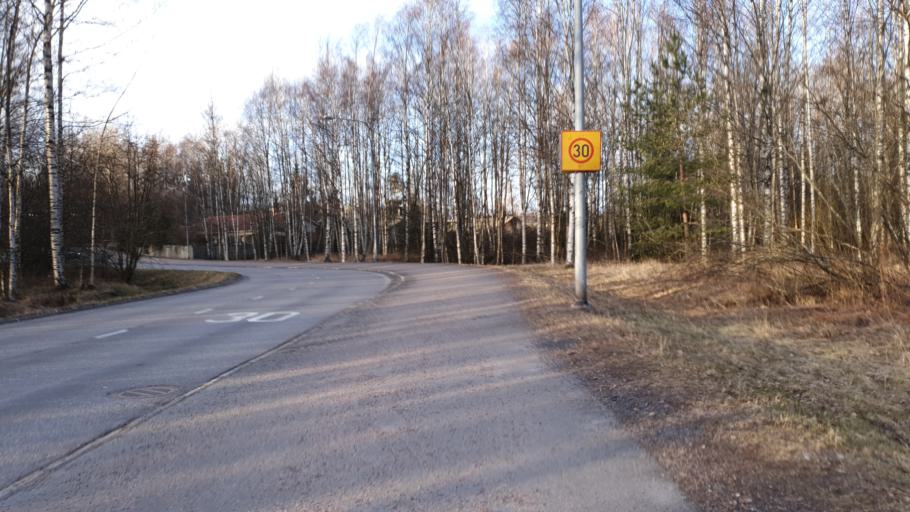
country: FI
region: Uusimaa
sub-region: Helsinki
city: Vantaa
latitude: 60.3072
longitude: 25.0050
